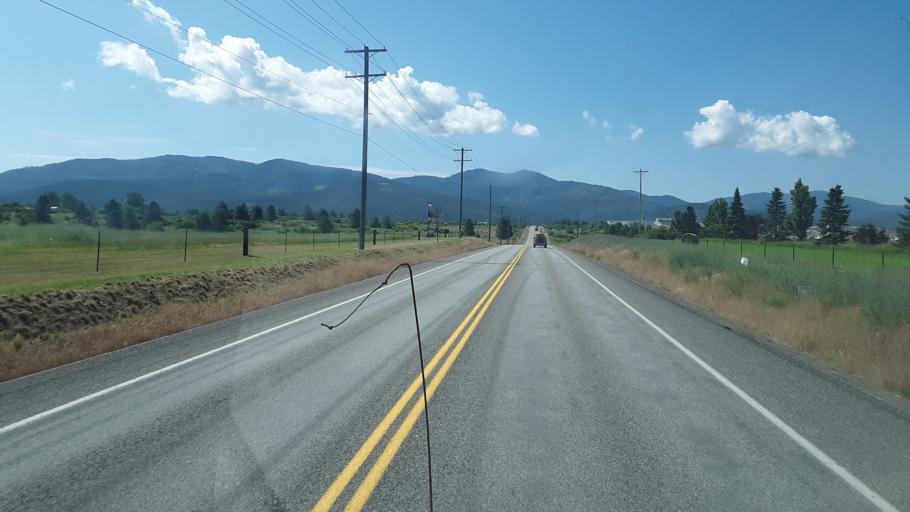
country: US
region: Idaho
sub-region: Kootenai County
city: Post Falls
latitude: 47.7302
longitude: -117.0018
